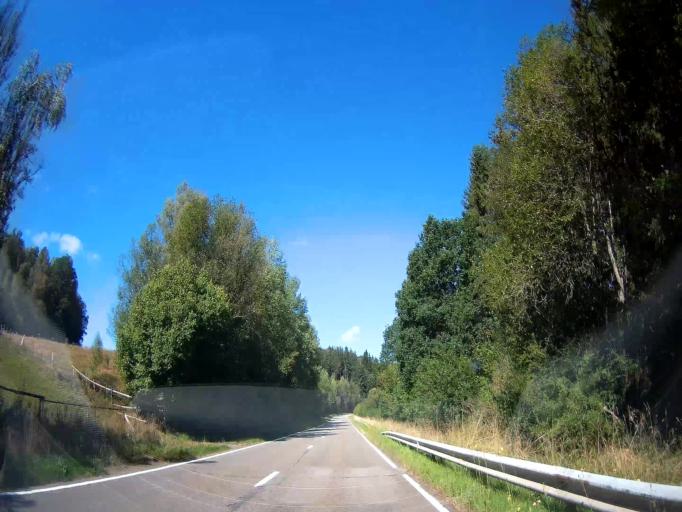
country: BE
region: Wallonia
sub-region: Province du Luxembourg
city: Bertogne
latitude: 50.1076
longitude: 5.6319
